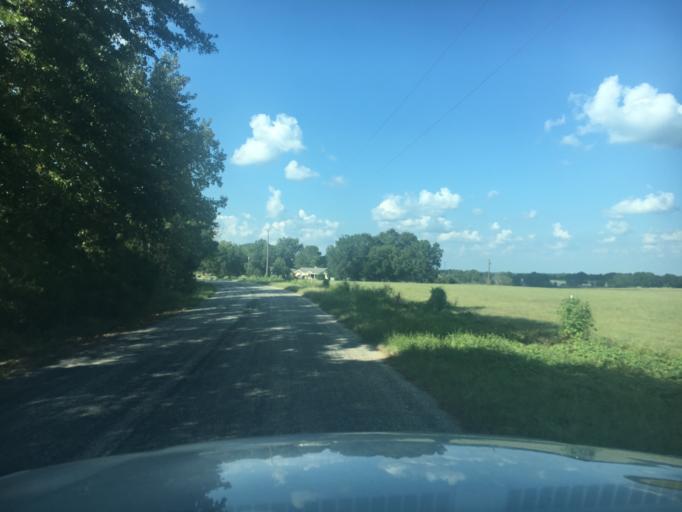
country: US
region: South Carolina
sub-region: Greenwood County
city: Ware Shoals
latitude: 34.4727
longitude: -82.2398
